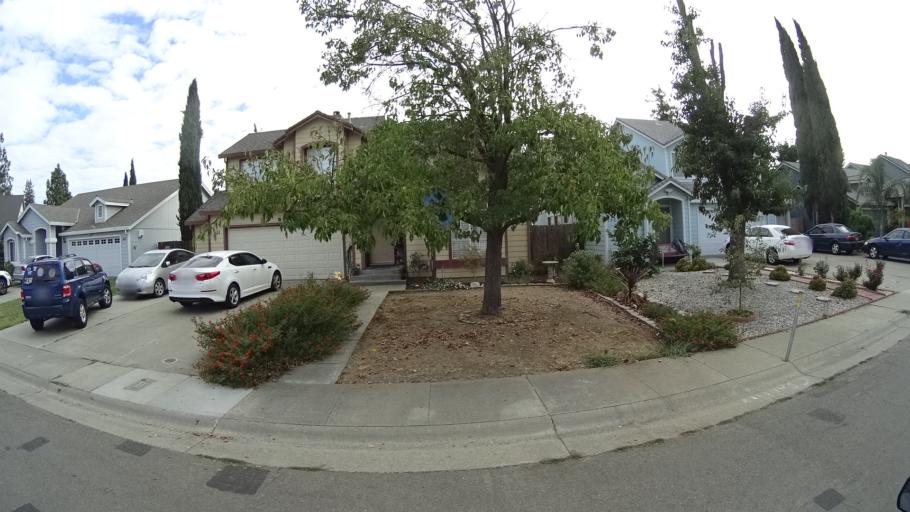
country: US
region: California
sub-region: Sacramento County
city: Laguna
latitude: 38.4482
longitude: -121.4207
